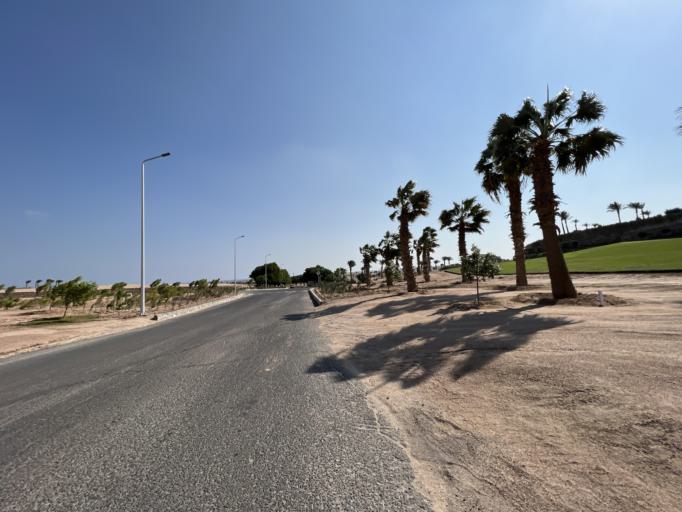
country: EG
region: Red Sea
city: Makadi Bay
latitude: 26.9856
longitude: 33.8871
